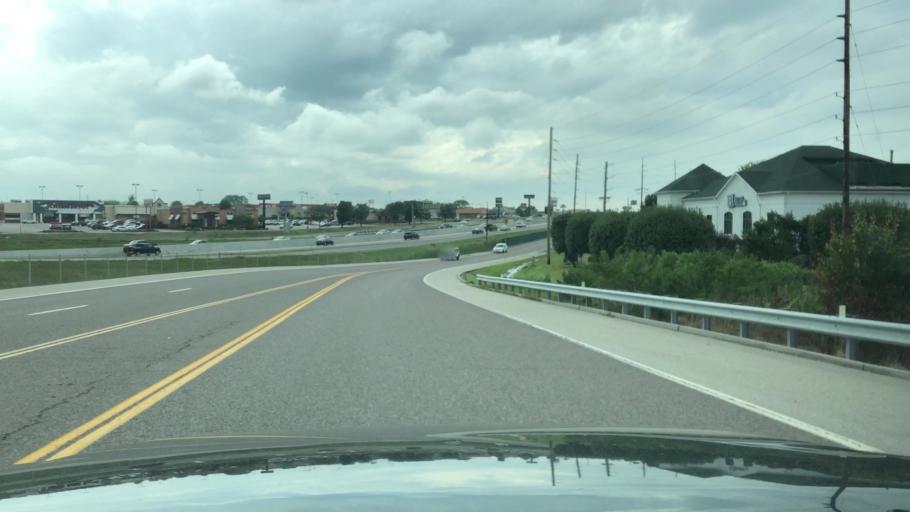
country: US
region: Missouri
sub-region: Saint Charles County
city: Saint Peters
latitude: 38.7951
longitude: -90.5659
